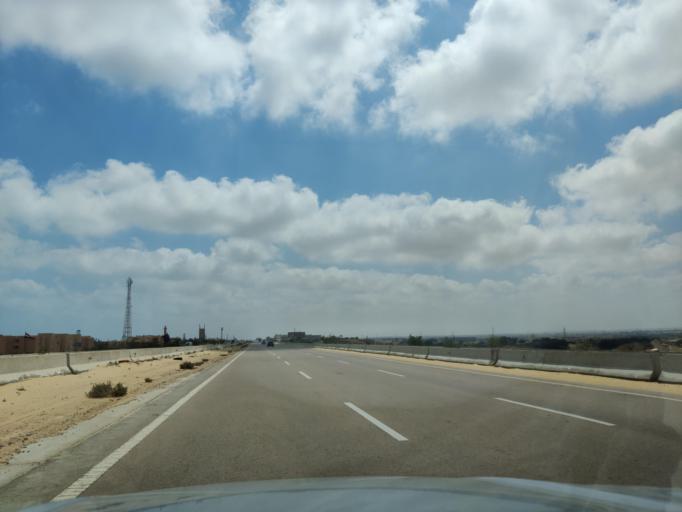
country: EG
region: Muhafazat Matruh
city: Al `Alamayn
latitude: 30.8169
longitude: 29.1437
